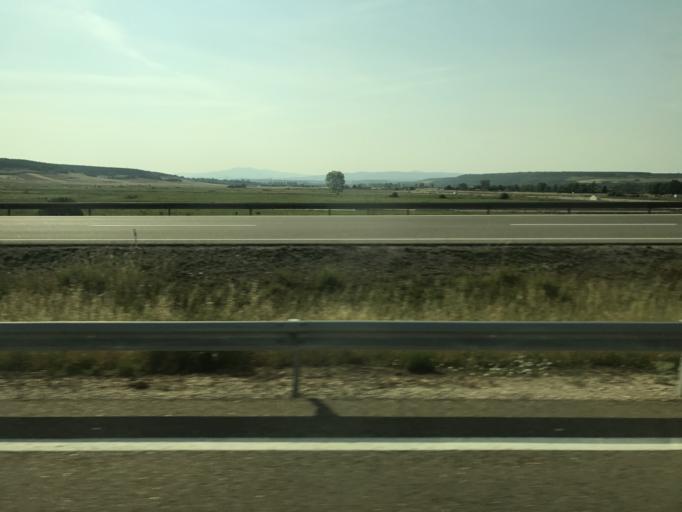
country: ES
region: Castille and Leon
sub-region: Provincia de Burgos
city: Cardenajimeno
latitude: 42.3444
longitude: -3.6056
